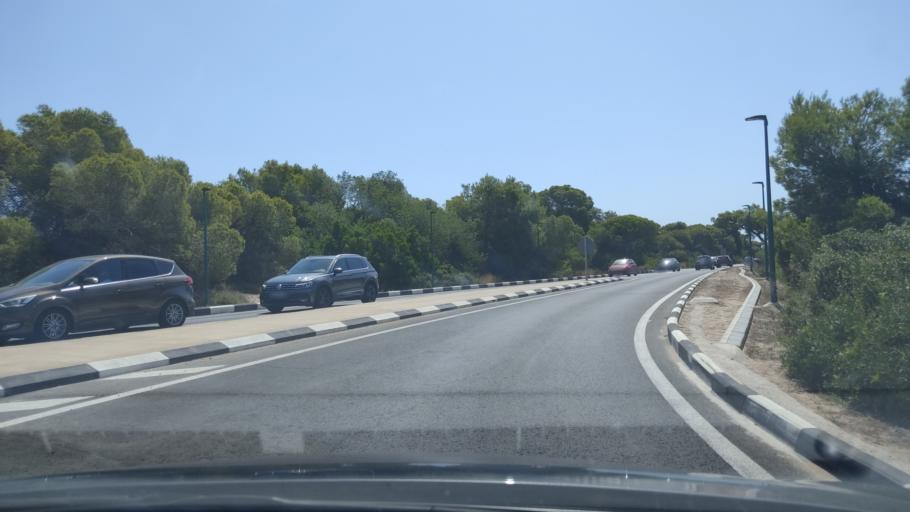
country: ES
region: Valencia
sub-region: Provincia de Valencia
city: Sollana
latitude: 39.3398
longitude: -0.3190
